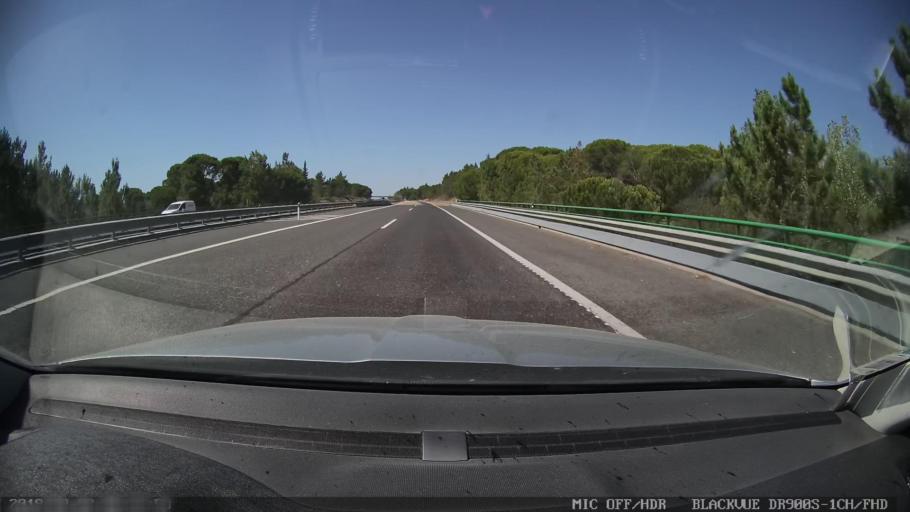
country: PT
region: Evora
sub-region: Vendas Novas
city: Vendas Novas
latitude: 38.6406
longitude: -8.4969
